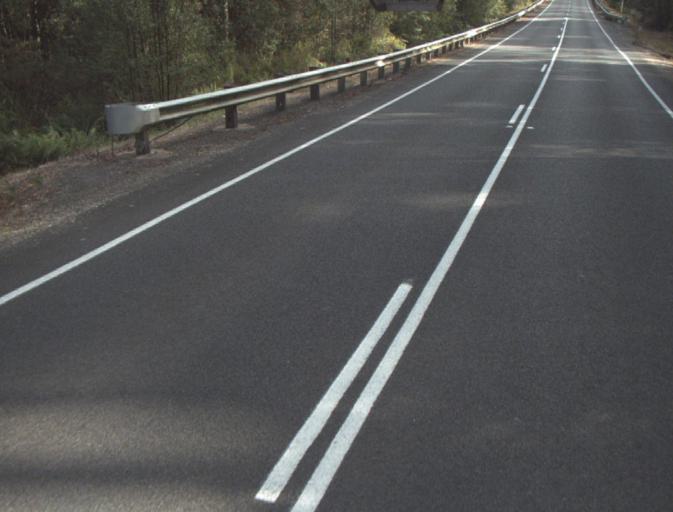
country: AU
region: Tasmania
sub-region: Launceston
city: Mayfield
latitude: -41.3068
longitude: 147.2043
